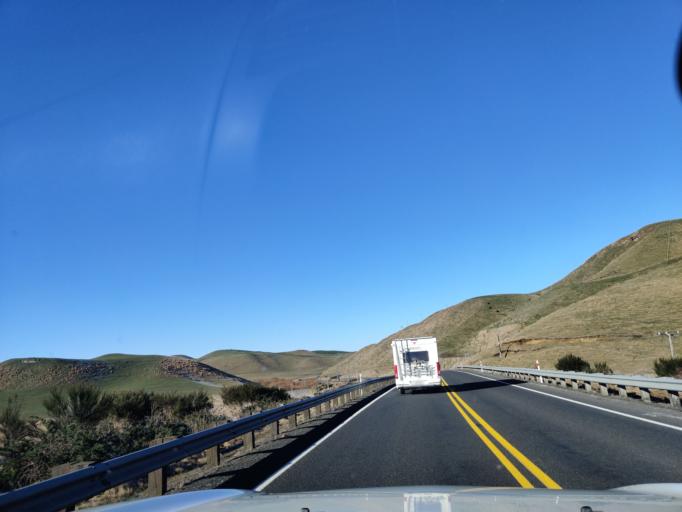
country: NZ
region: Manawatu-Wanganui
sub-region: Ruapehu District
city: Waiouru
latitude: -39.4997
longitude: 175.6740
